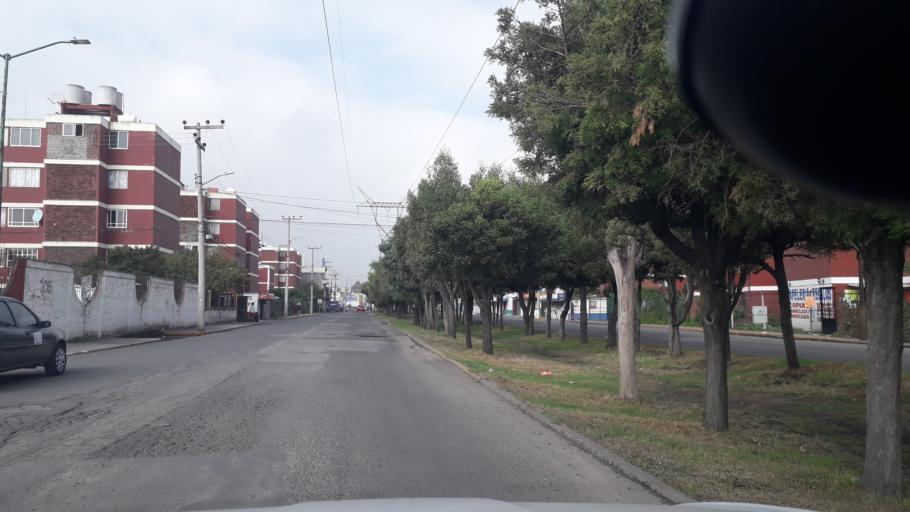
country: MX
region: Mexico
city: Coacalco
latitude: 19.6444
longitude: -99.0850
